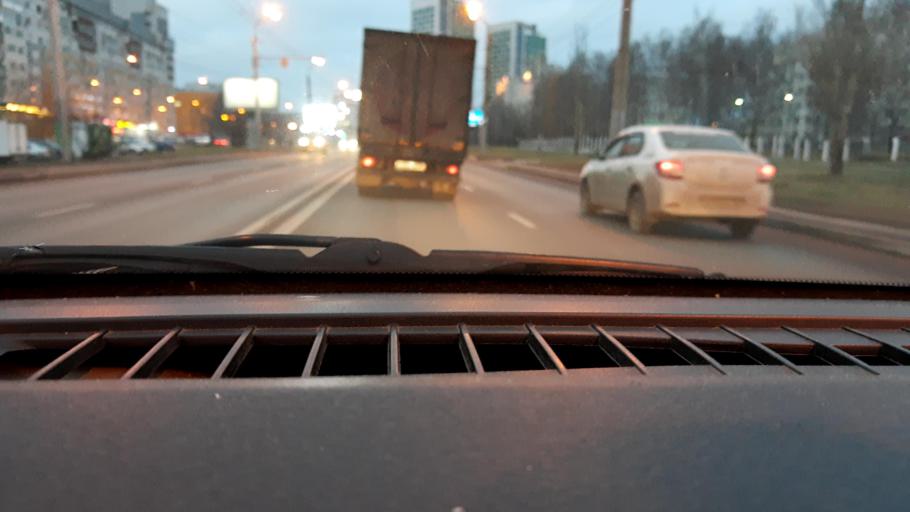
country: RU
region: Nizjnij Novgorod
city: Afonino
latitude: 56.3022
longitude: 44.0822
